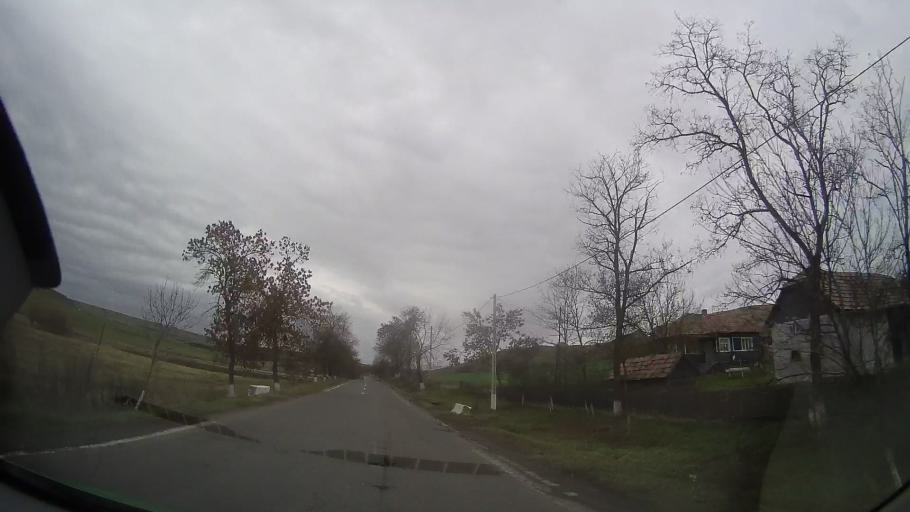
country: RO
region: Bistrita-Nasaud
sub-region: Comuna Urmenis
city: Urmenis
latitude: 46.7610
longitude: 24.3930
